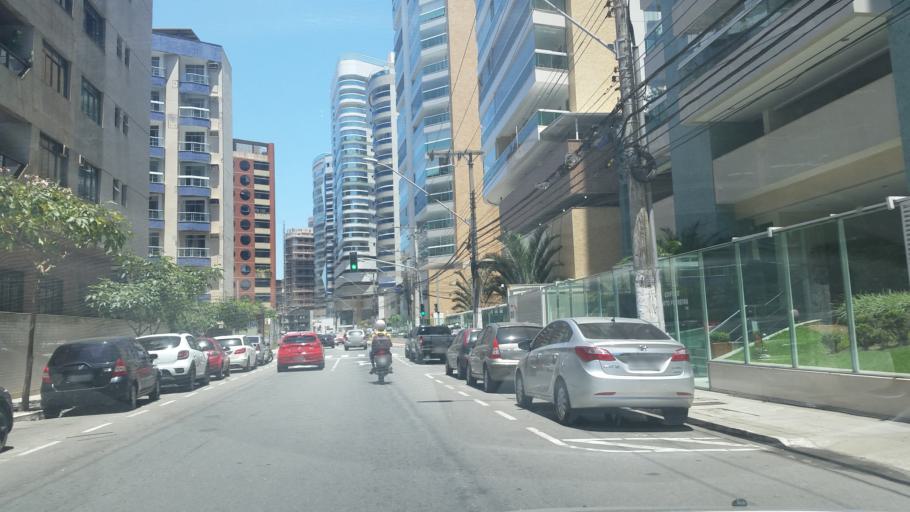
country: BR
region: Espirito Santo
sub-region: Vila Velha
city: Vila Velha
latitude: -20.3336
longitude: -40.2806
